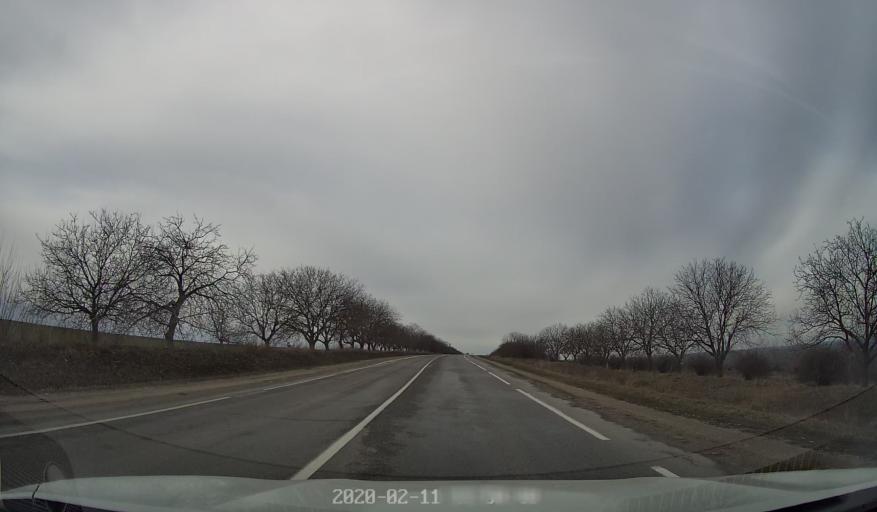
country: MD
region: Drochia
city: Drochia
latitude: 47.8584
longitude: 27.7634
